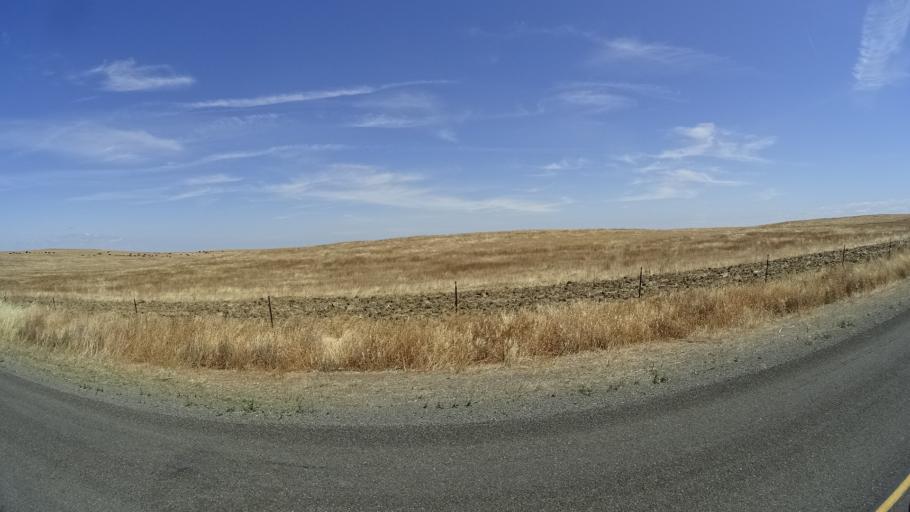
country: US
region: California
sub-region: Kings County
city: Kettleman City
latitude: 35.8226
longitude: -119.9078
